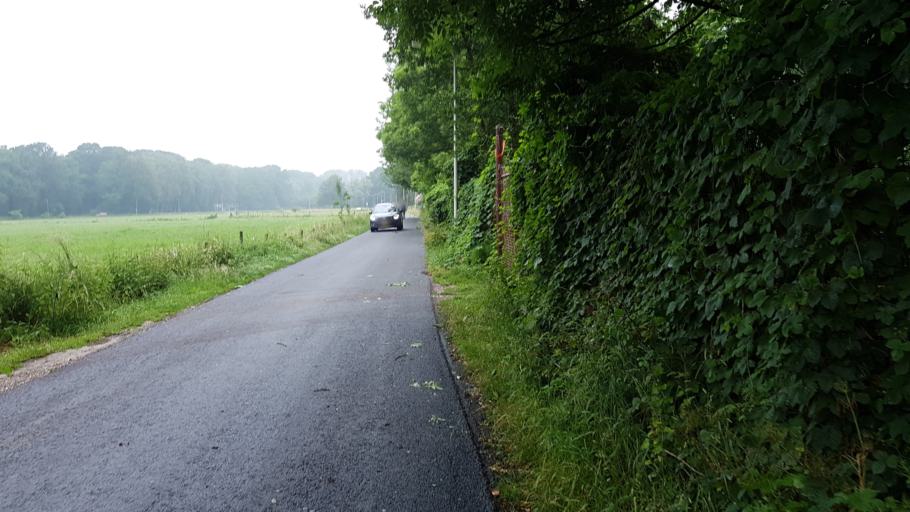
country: NL
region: Overijssel
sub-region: Gemeente Hengelo
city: Hengelo
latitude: 52.2791
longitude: 6.7977
